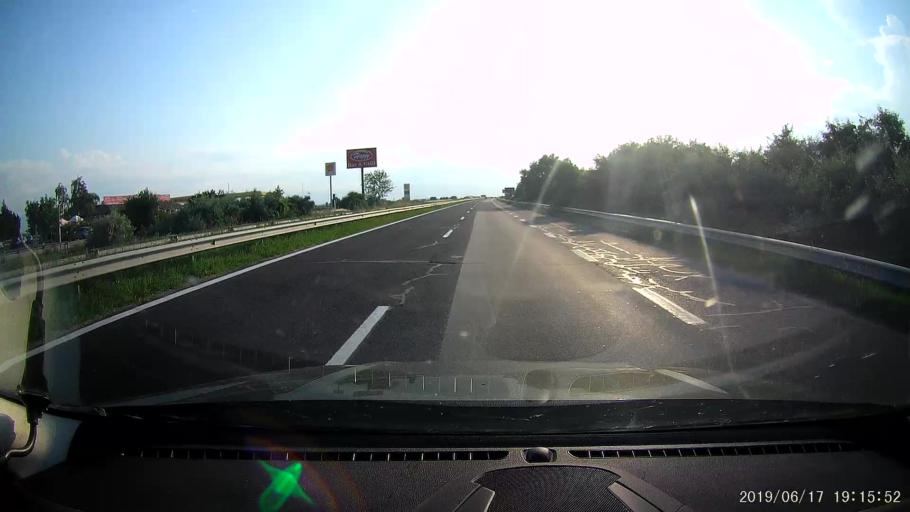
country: BG
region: Plovdiv
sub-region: Obshtina Suedinenie
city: Suedinenie
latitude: 42.1983
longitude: 24.6347
